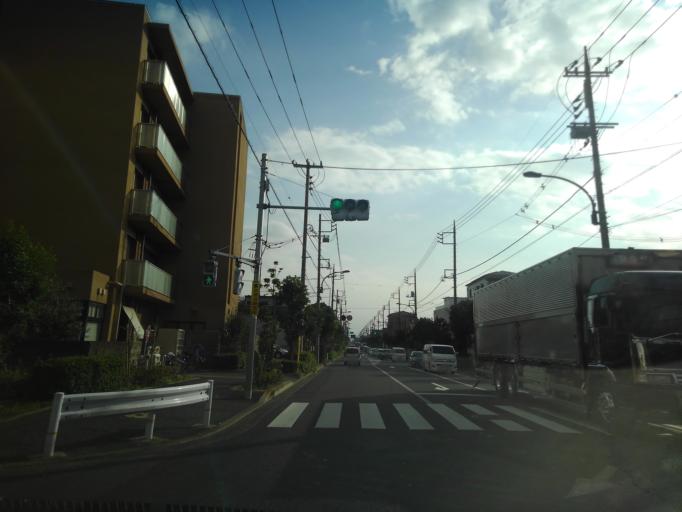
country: JP
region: Tokyo
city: Kokubunji
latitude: 35.7266
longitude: 139.4979
